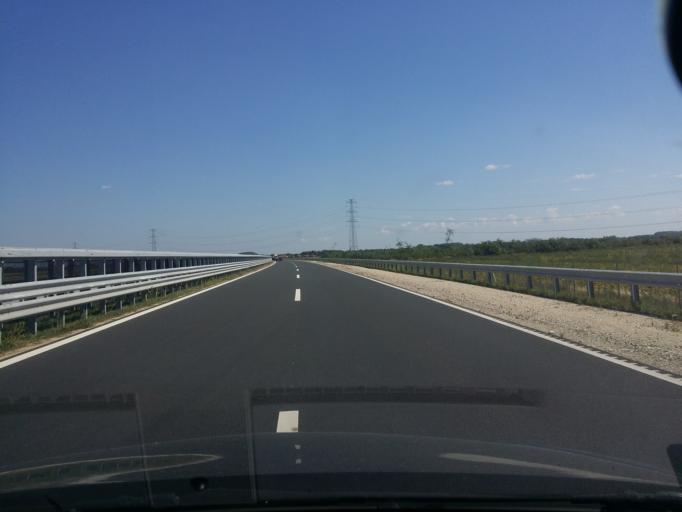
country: HU
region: Vas
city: Repcelak
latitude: 47.3909
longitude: 16.9903
